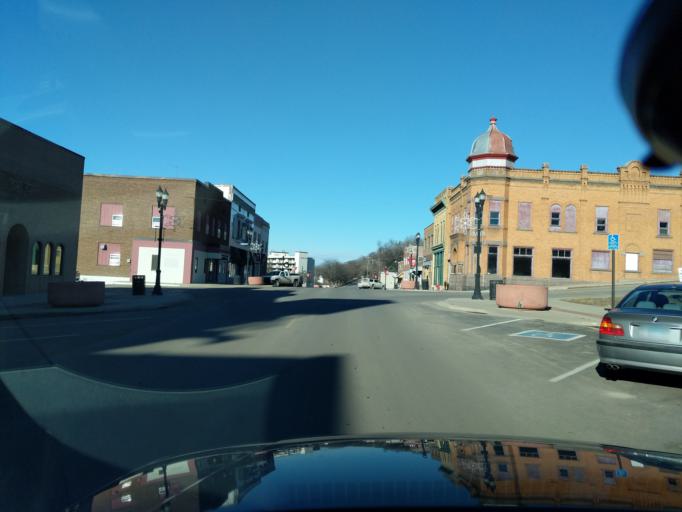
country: US
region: Minnesota
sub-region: Chippewa County
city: Montevideo
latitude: 44.9469
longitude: -95.7247
